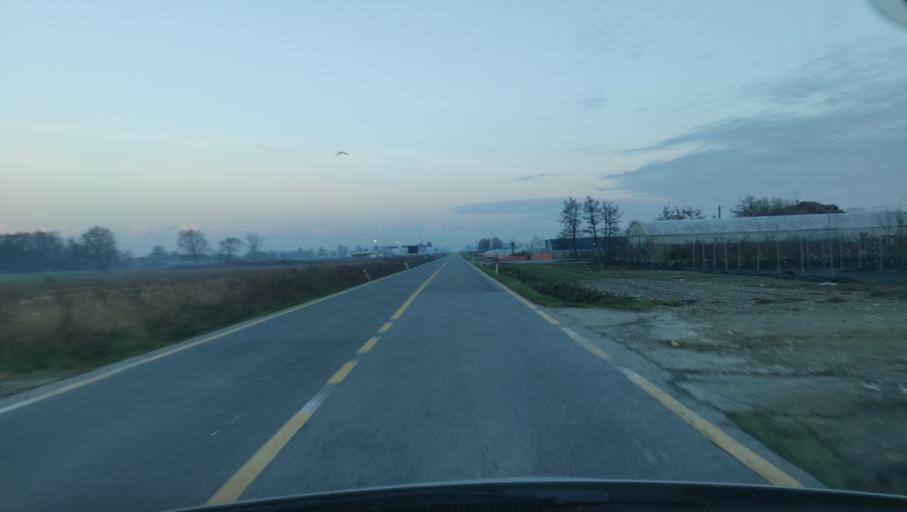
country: IT
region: Piedmont
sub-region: Provincia di Torino
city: Montanaro
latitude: 45.2383
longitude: 7.8912
